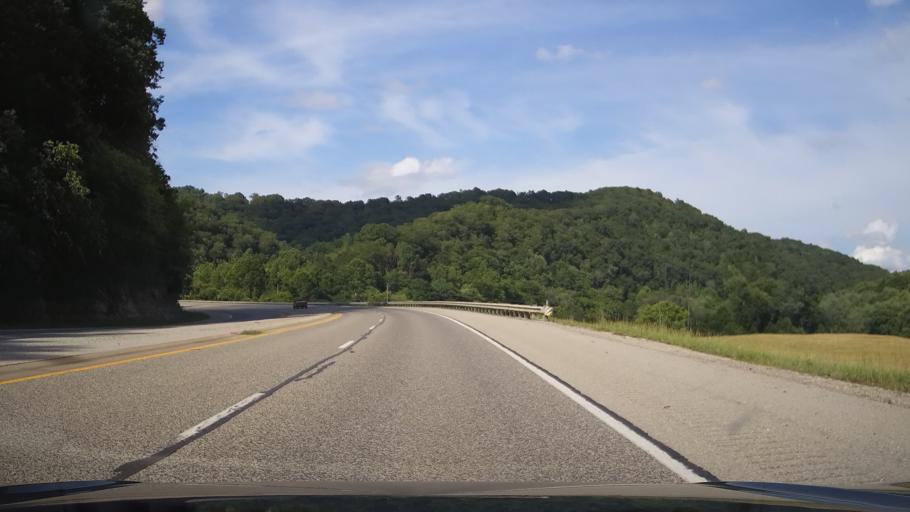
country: US
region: Kentucky
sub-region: Lawrence County
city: Louisa
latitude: 38.0201
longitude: -82.6533
